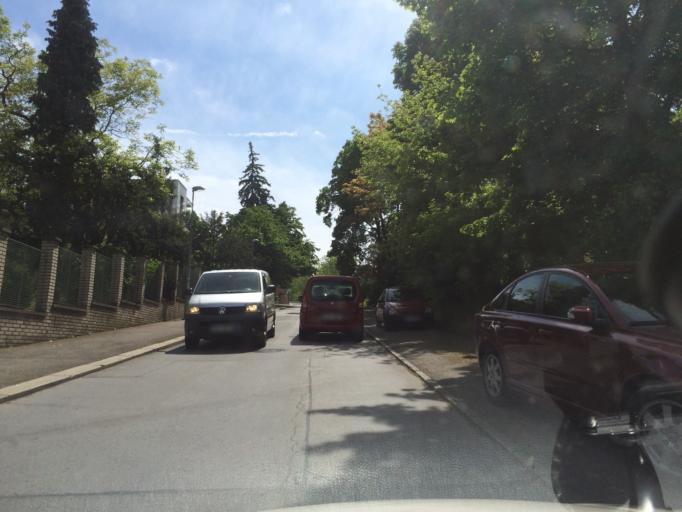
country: CZ
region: Praha
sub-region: Praha 1
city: Mala Strana
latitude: 50.0971
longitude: 14.3879
